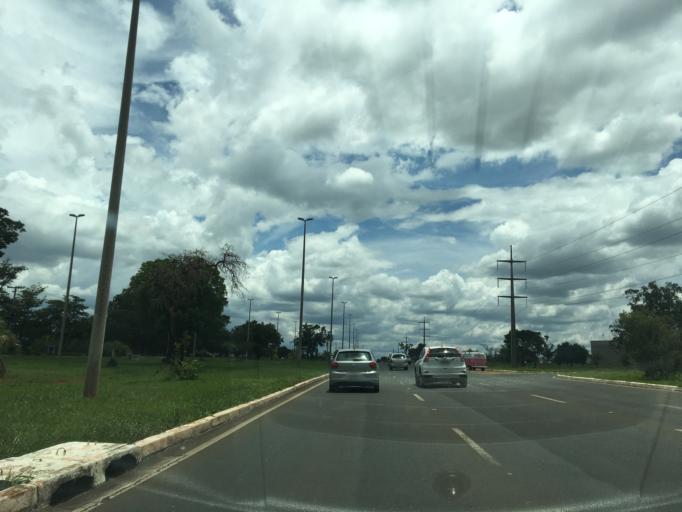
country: BR
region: Federal District
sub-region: Brasilia
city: Brasilia
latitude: -15.7663
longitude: -47.8630
